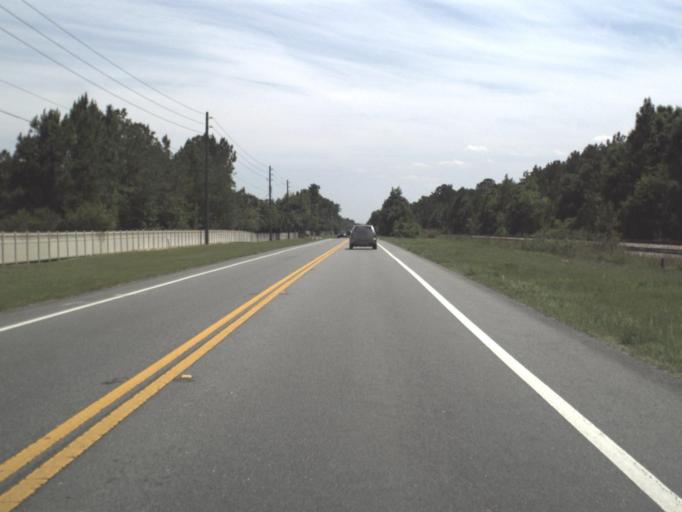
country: US
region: Florida
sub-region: Nassau County
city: Yulee
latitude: 30.5263
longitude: -81.6224
